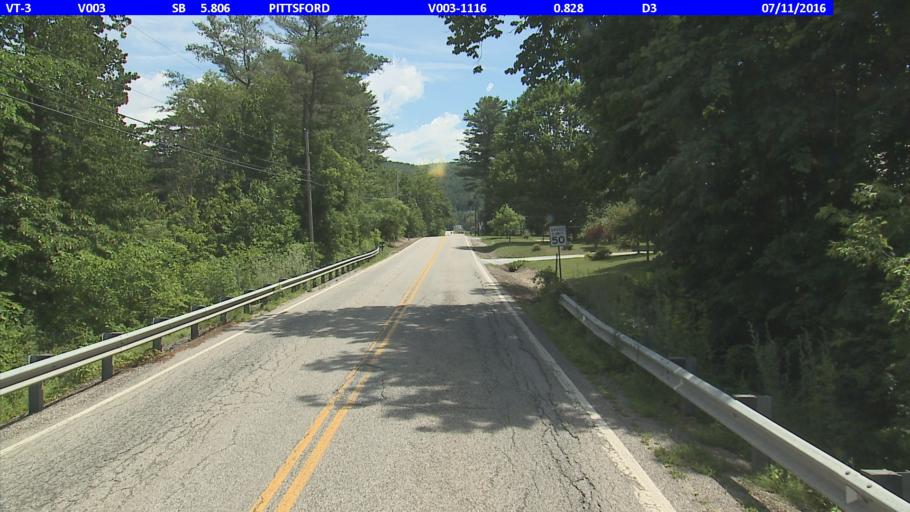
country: US
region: Vermont
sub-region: Rutland County
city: West Rutland
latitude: 43.6770
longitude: -73.0280
